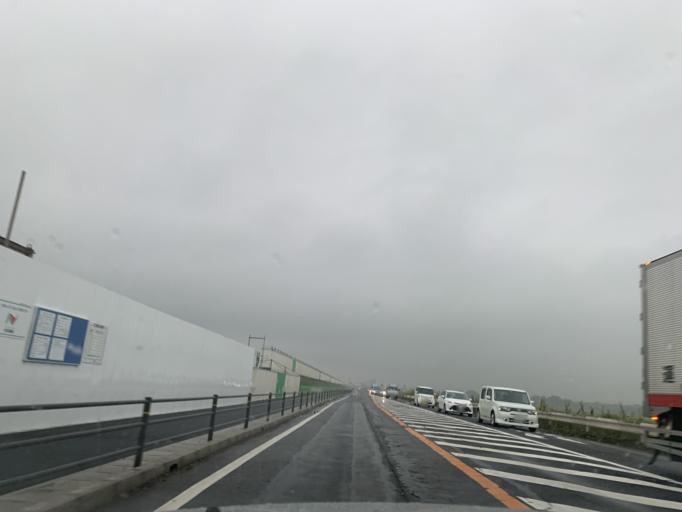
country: JP
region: Chiba
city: Nagareyama
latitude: 35.9035
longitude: 139.8910
